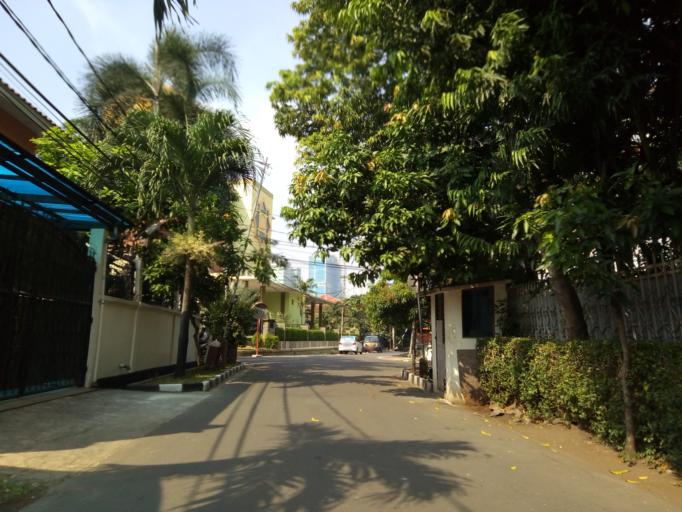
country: ID
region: Jakarta Raya
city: Jakarta
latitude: -6.2068
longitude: 106.8346
